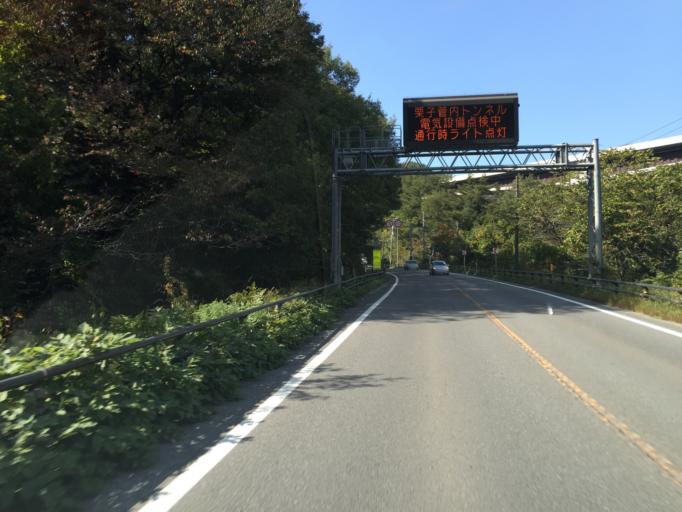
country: JP
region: Fukushima
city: Fukushima-shi
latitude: 37.8406
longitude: 140.3654
